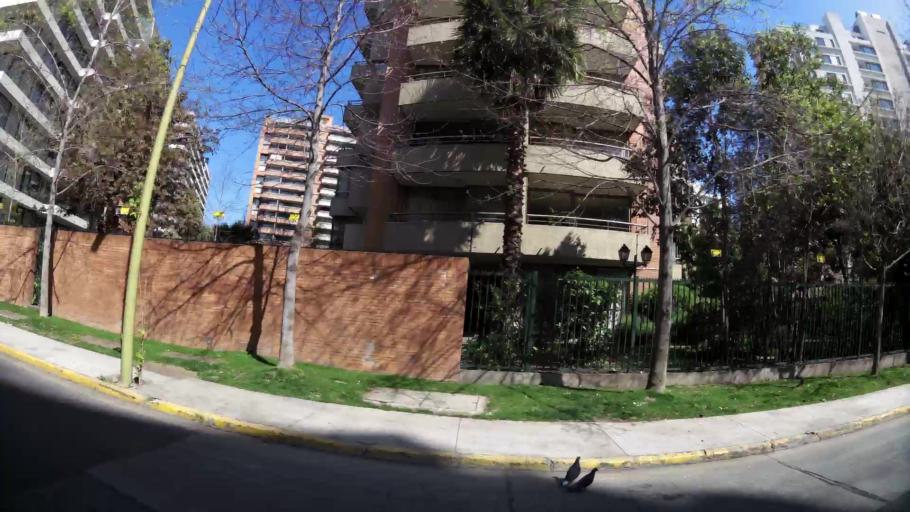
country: CL
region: Santiago Metropolitan
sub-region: Provincia de Santiago
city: Villa Presidente Frei, Nunoa, Santiago, Chile
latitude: -33.4119
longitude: -70.5886
